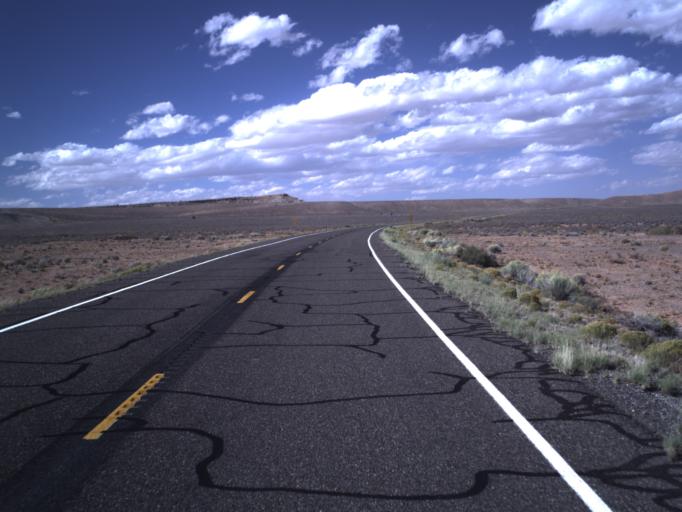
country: US
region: Utah
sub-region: Wayne County
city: Loa
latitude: 38.0988
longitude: -110.6224
